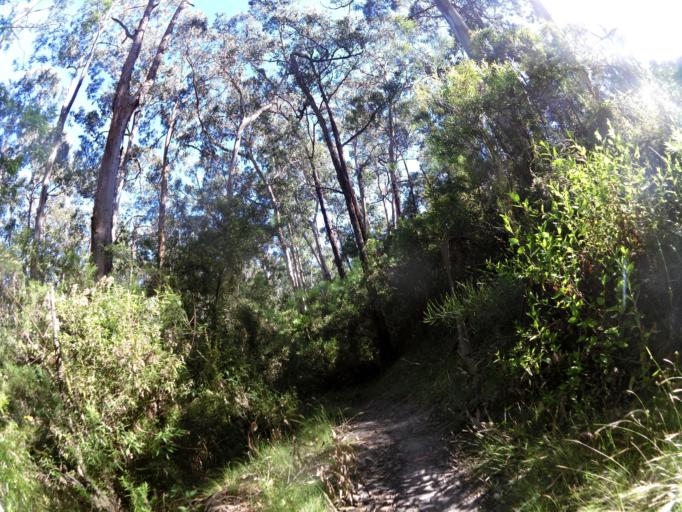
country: AU
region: Victoria
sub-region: Colac-Otway
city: Apollo Bay
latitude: -38.5355
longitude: 143.7287
